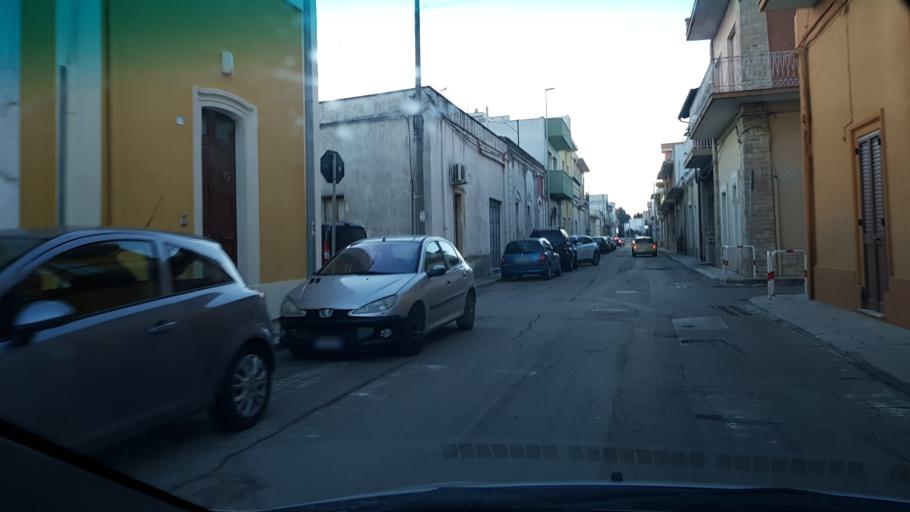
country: IT
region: Apulia
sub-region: Provincia di Brindisi
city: San Pietro Vernotico
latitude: 40.4889
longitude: 17.9927
